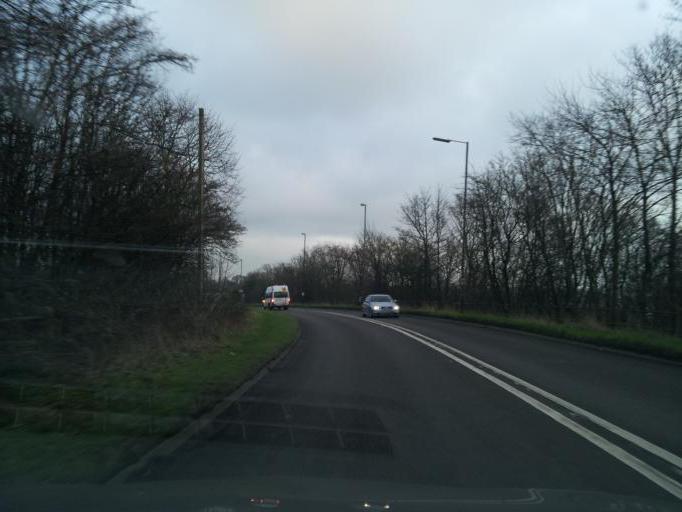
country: GB
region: England
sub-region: Derbyshire
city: Etwall
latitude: 52.8535
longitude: -1.5830
